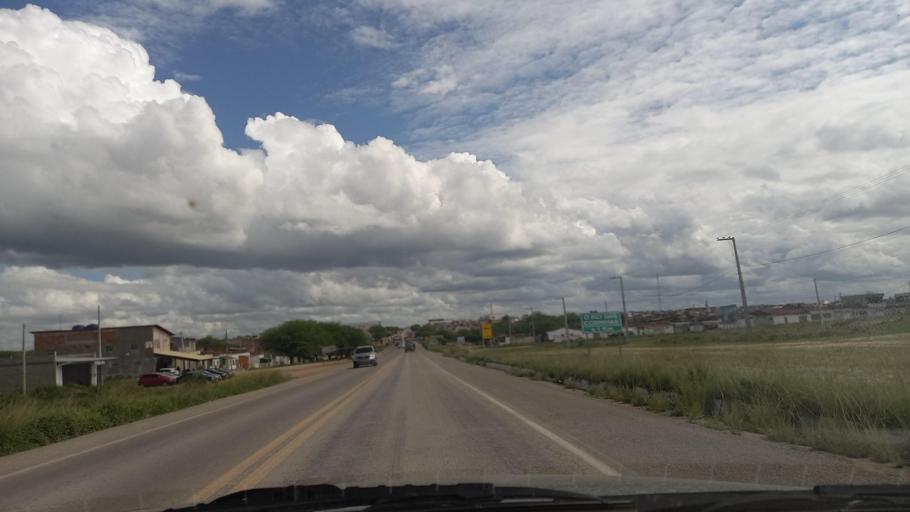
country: BR
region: Pernambuco
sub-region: Cachoeirinha
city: Cachoeirinha
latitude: -8.4856
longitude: -36.2278
